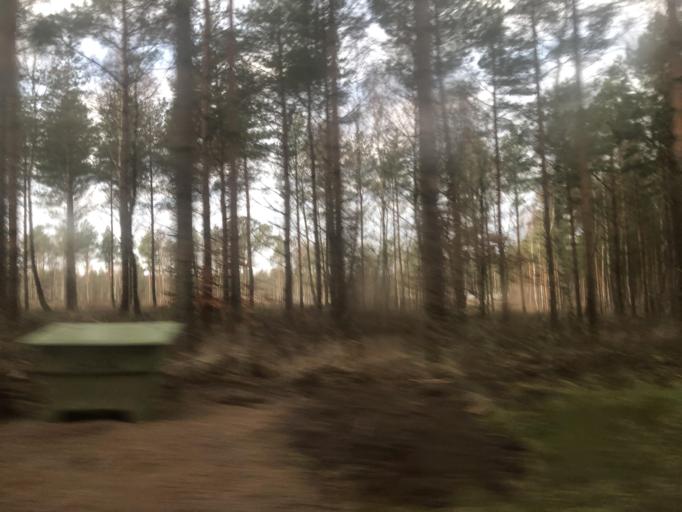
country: SE
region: Skane
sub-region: Sjobo Kommun
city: Blentarp
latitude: 55.6189
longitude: 13.5488
